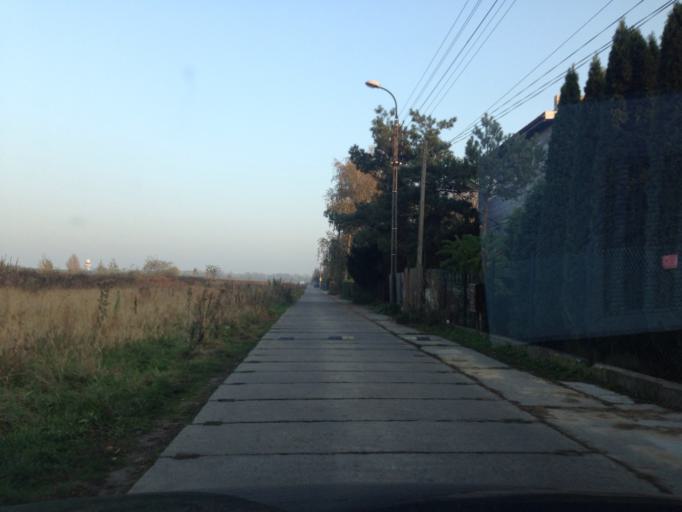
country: PL
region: Masovian Voivodeship
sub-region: Powiat pruszkowski
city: Rybie
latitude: 52.1622
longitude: 20.9371
